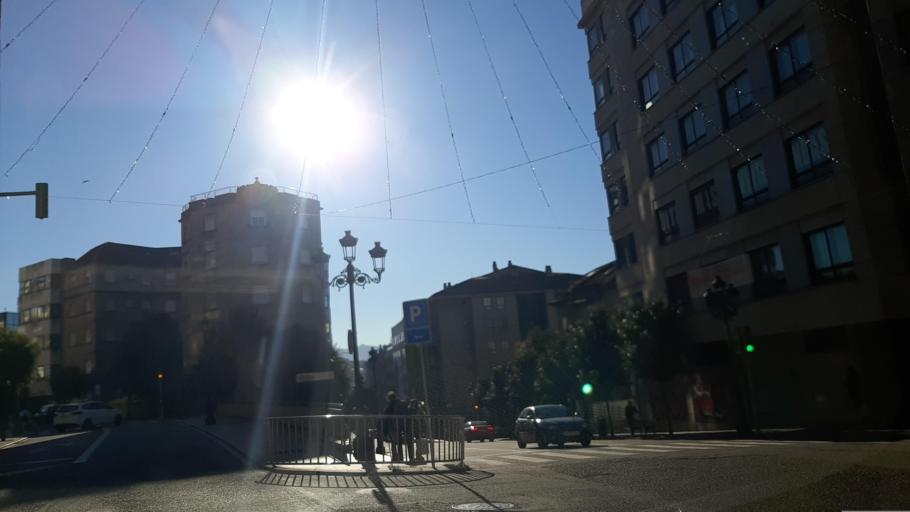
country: ES
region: Galicia
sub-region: Provincia de Pontevedra
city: Vigo
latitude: 42.2282
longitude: -8.7323
